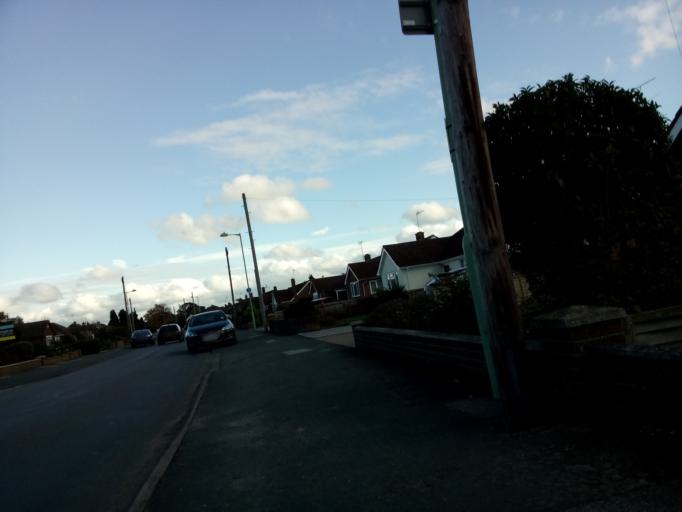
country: GB
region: England
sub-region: Suffolk
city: Kesgrave
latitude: 52.0578
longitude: 1.2301
